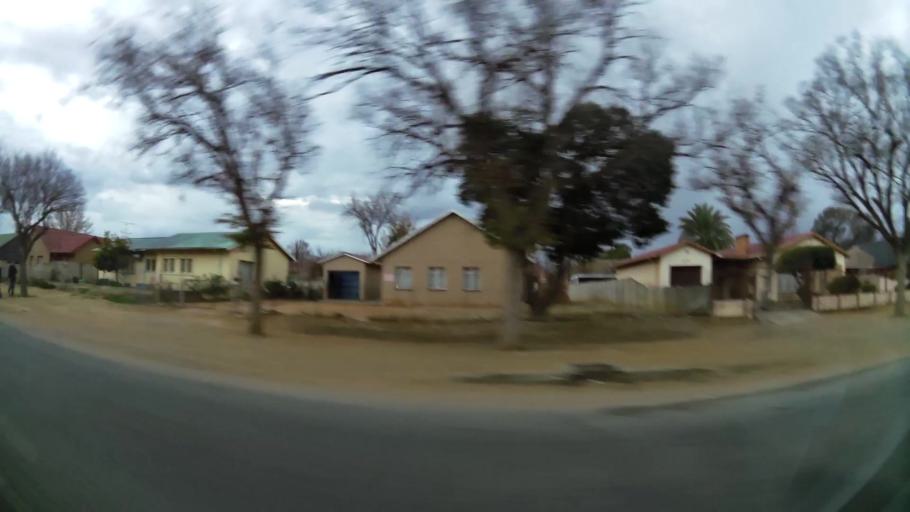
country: ZA
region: Orange Free State
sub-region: Lejweleputswa District Municipality
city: Welkom
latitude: -27.9783
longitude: 26.7561
